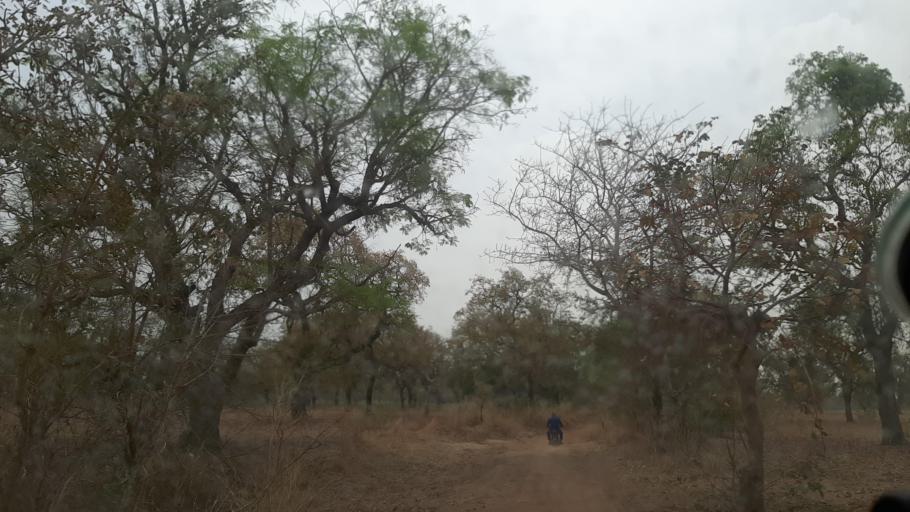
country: BF
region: Boucle du Mouhoun
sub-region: Province des Banwa
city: Salanso
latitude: 11.8528
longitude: -4.4281
